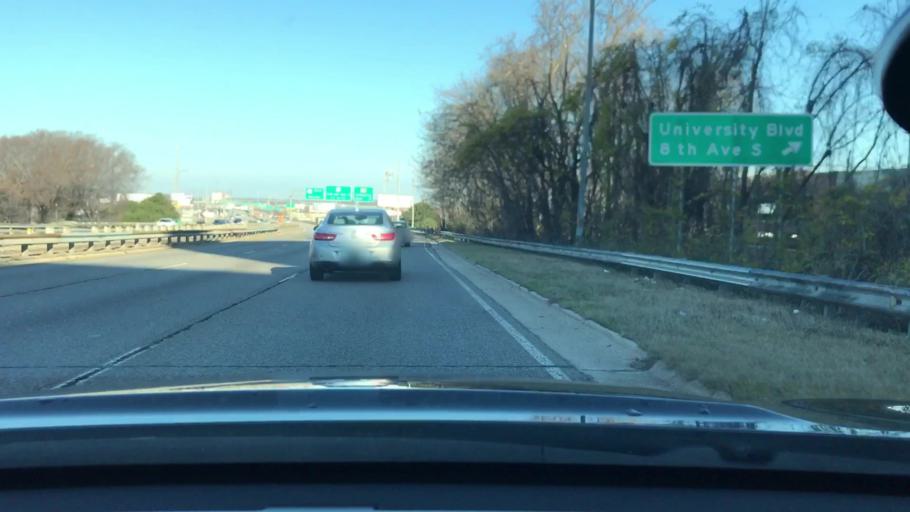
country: US
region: Alabama
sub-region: Jefferson County
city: Birmingham
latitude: 33.5077
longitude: -86.7903
